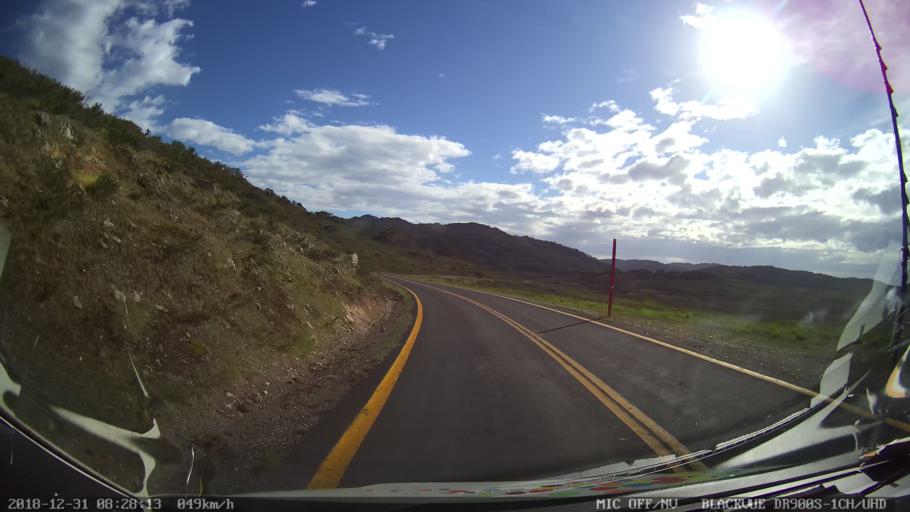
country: AU
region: New South Wales
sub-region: Snowy River
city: Jindabyne
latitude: -36.4291
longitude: 148.3442
